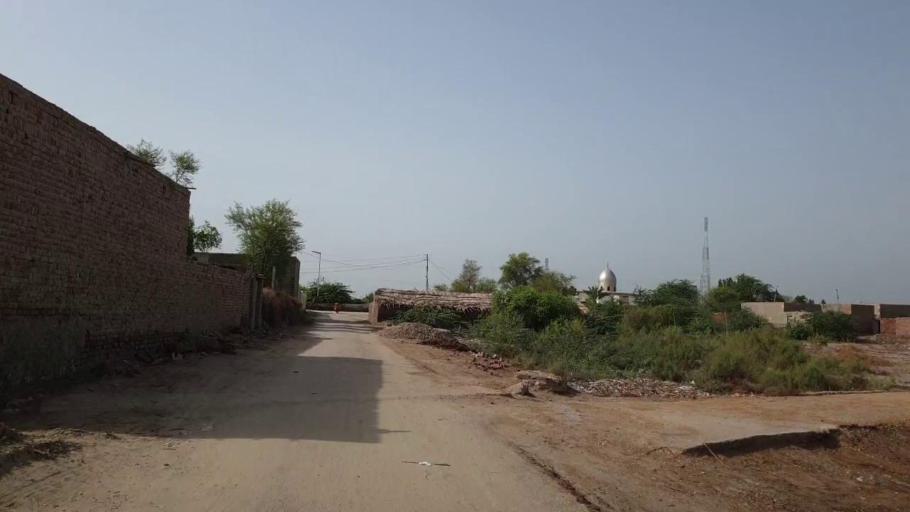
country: PK
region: Sindh
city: Jam Sahib
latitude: 26.2991
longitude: 68.6317
